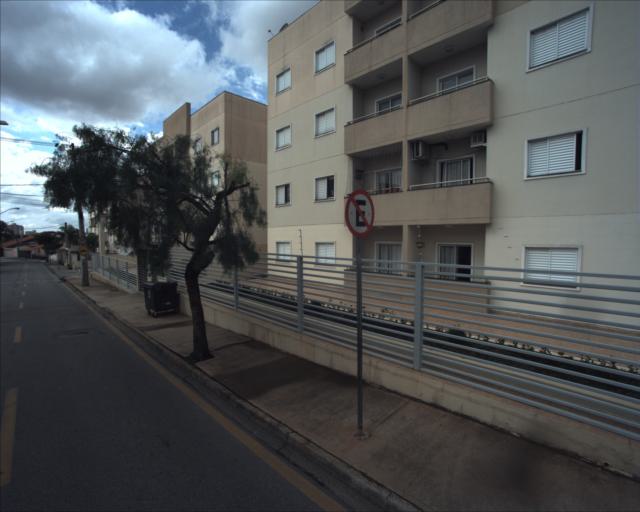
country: BR
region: Sao Paulo
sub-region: Sorocaba
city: Sorocaba
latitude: -23.5227
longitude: -47.4854
